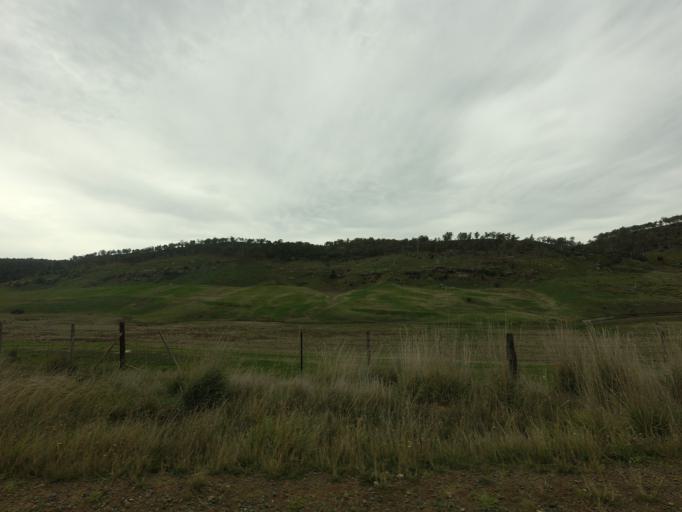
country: AU
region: Tasmania
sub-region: Derwent Valley
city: New Norfolk
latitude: -42.4018
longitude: 146.9201
